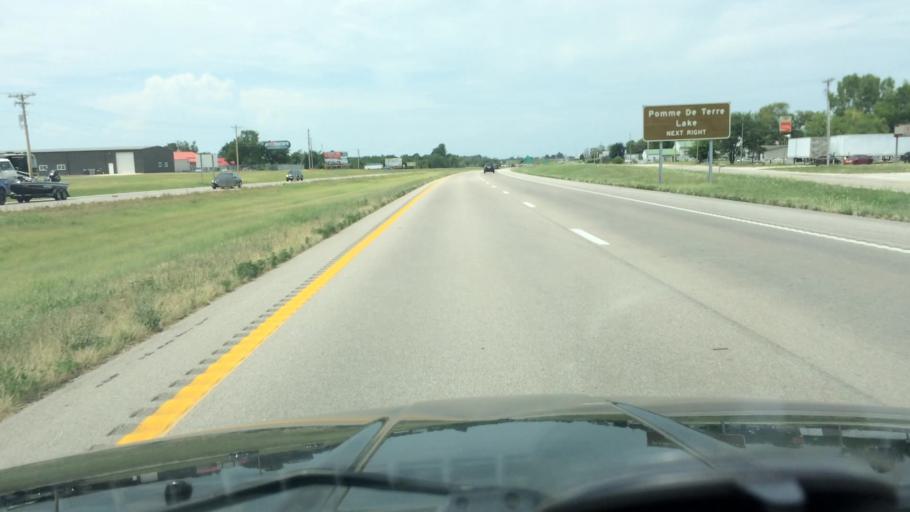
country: US
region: Missouri
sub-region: Polk County
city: Bolivar
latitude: 37.5622
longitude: -93.3923
